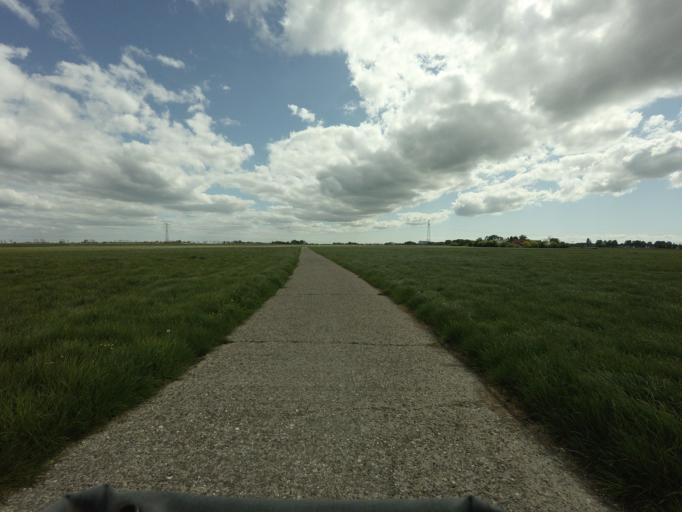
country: NL
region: Friesland
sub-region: Sudwest Fryslan
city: Bolsward
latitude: 53.0761
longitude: 5.5489
